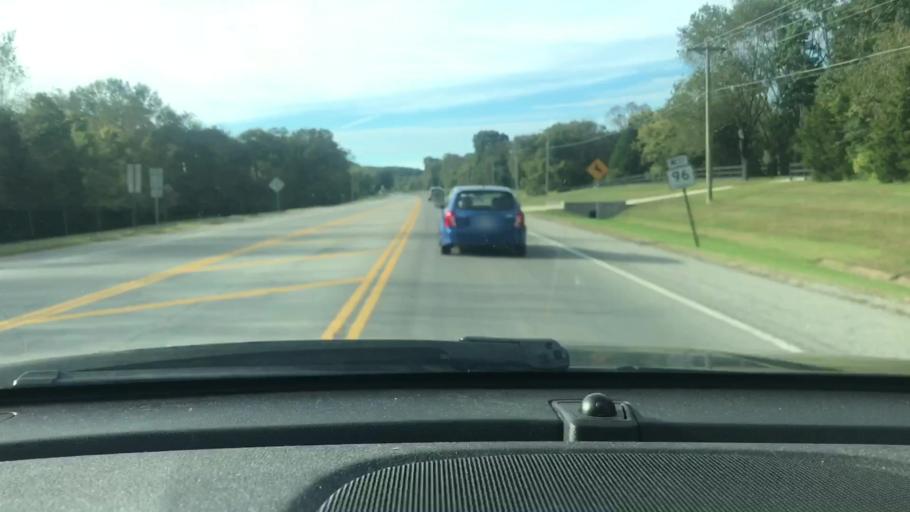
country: US
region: Tennessee
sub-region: Williamson County
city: Franklin
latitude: 35.9496
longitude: -86.9497
